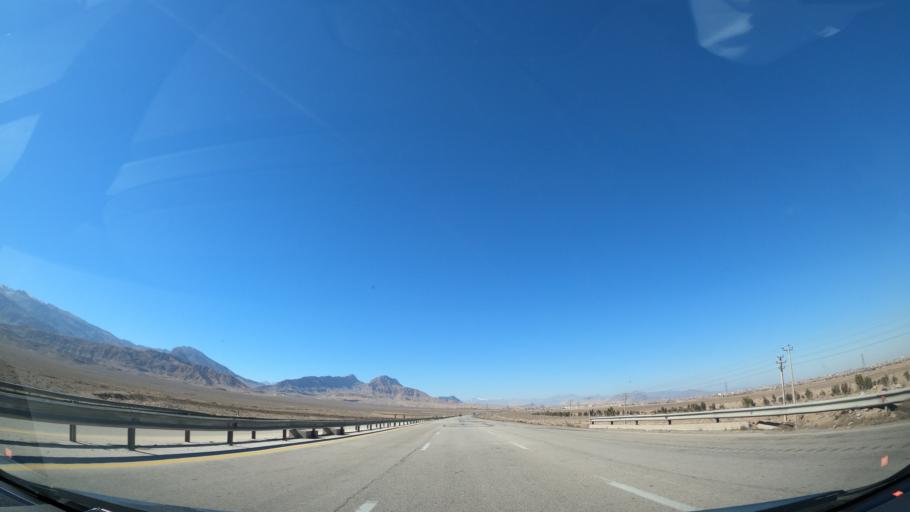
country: IR
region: Isfahan
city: Kashan
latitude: 33.9121
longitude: 51.4207
